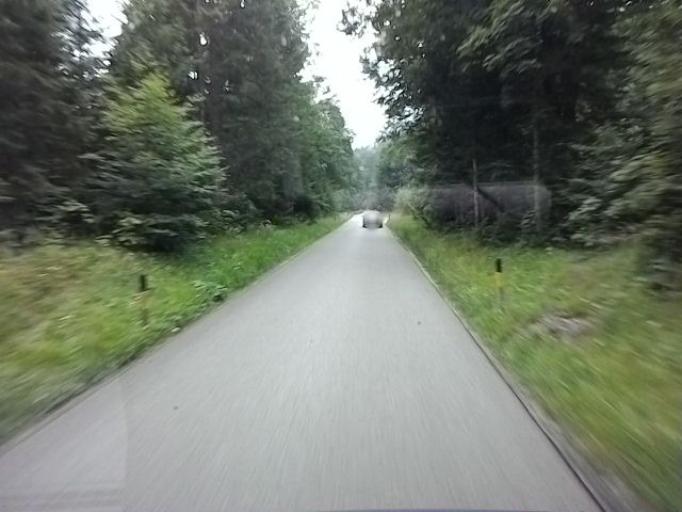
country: DE
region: Bavaria
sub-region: Upper Bavaria
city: Jachenau
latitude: 47.5480
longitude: 11.3778
